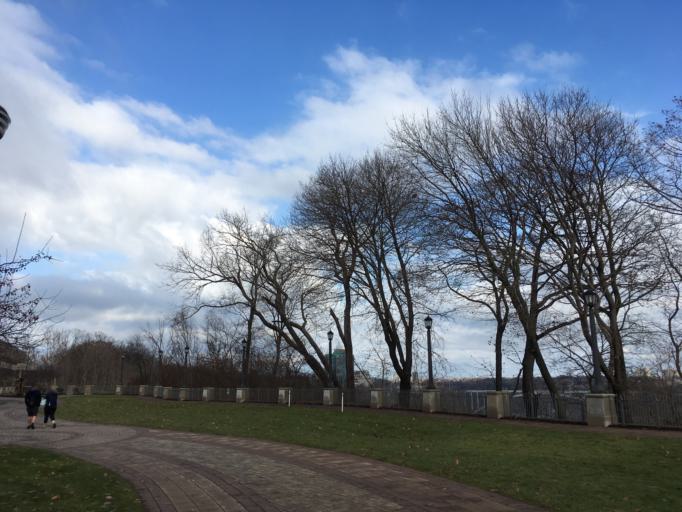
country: CA
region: Ontario
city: Niagara Falls
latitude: 43.0823
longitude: -79.0793
